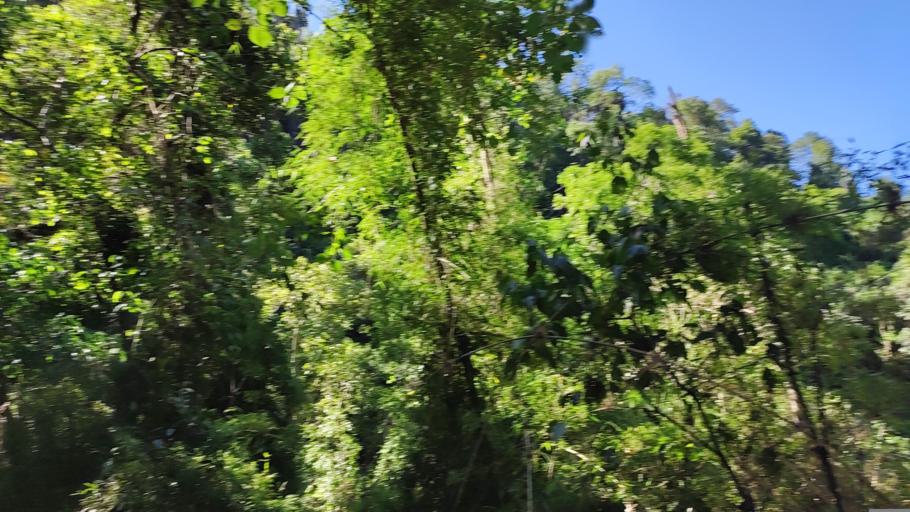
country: AR
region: Misiones
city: Dos de Mayo
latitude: -26.9931
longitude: -54.6306
